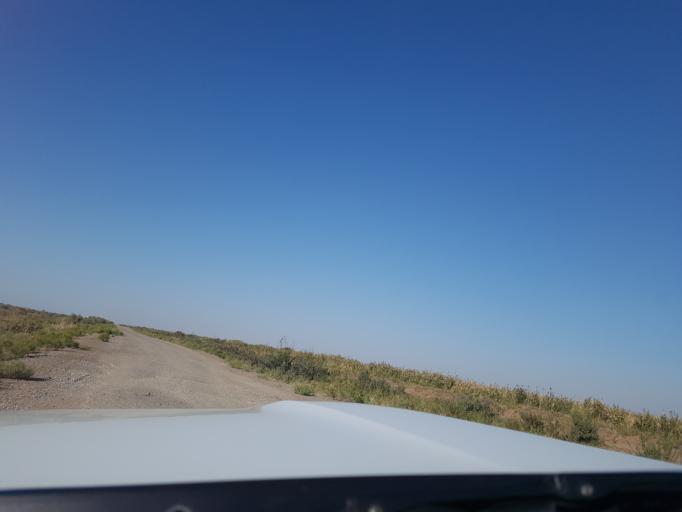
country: IR
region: Razavi Khorasan
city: Sarakhs
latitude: 36.9498
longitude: 61.3797
